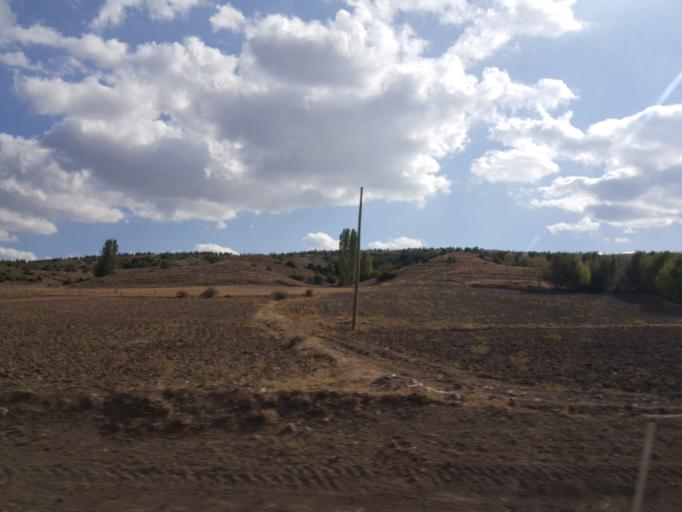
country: TR
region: Tokat
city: Sulusaray
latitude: 39.9889
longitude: 36.0026
